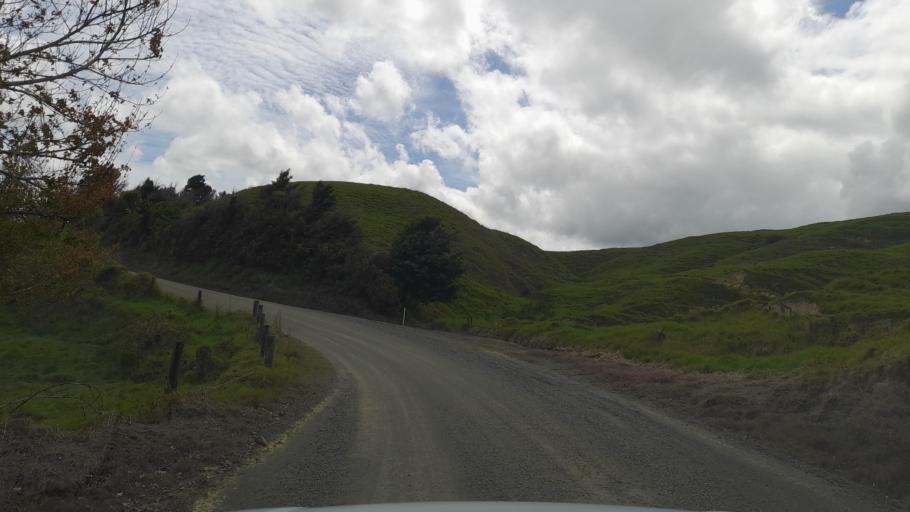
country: NZ
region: Auckland
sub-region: Auckland
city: Wellsford
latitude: -36.1937
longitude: 174.3398
